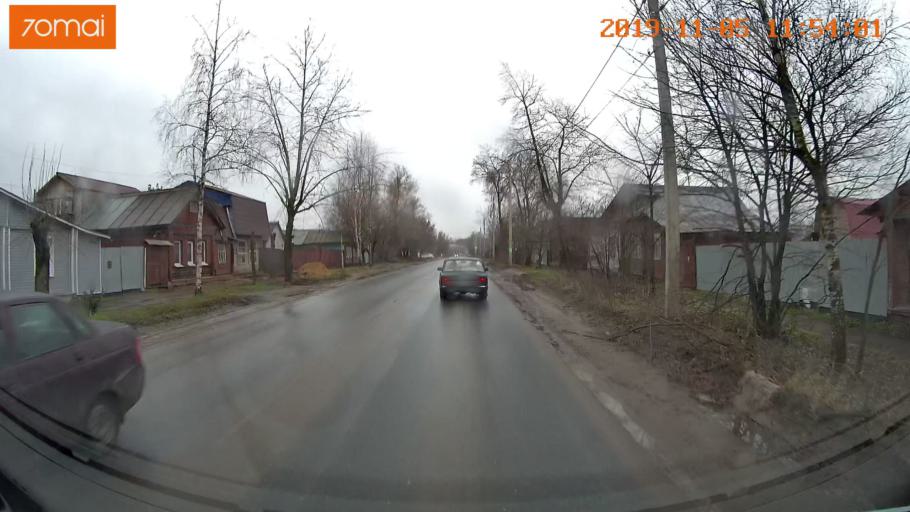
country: RU
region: Ivanovo
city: Bogorodskoye
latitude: 56.9934
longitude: 41.0308
